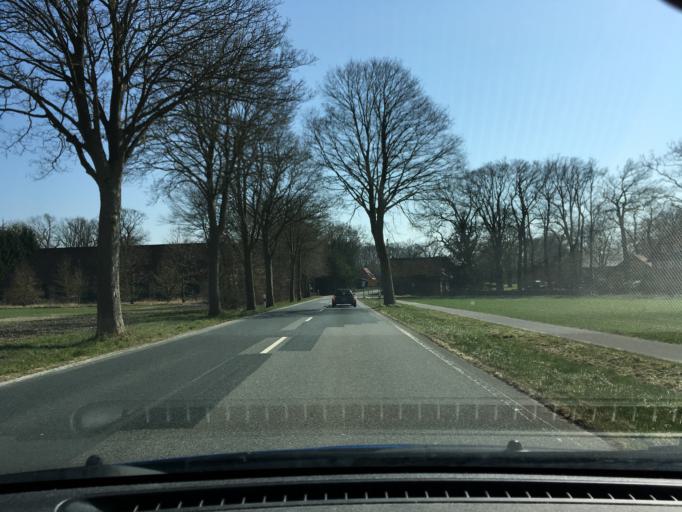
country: DE
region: Lower Saxony
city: Wriedel
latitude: 53.0555
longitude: 10.2905
